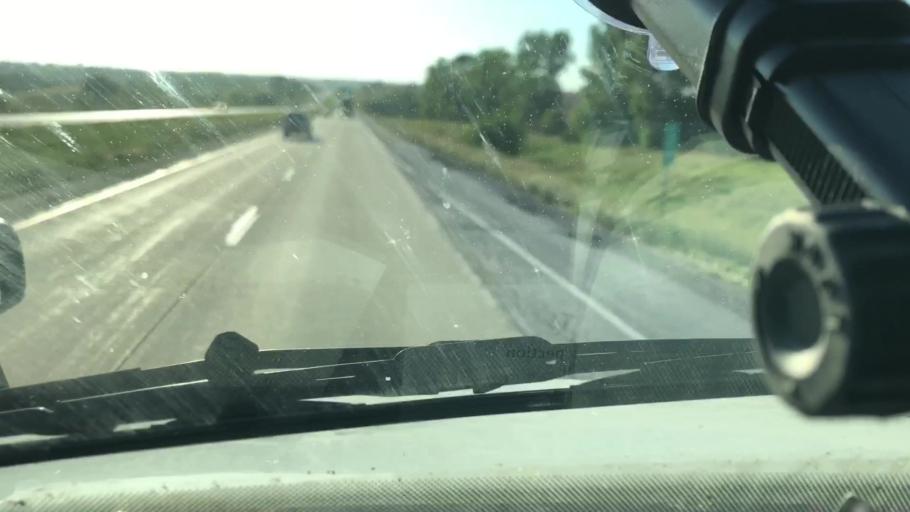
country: US
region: Iowa
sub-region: Pottawattamie County
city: Avoca
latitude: 41.4981
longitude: -95.5533
